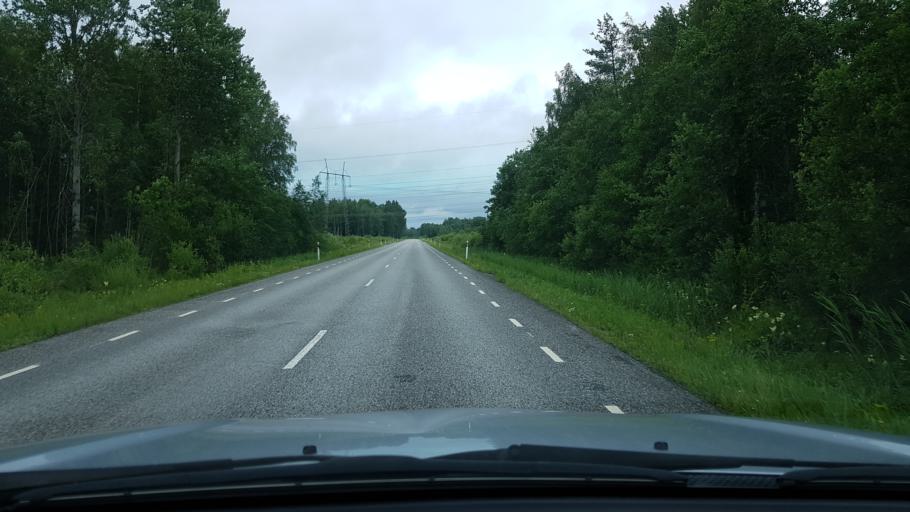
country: EE
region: Ida-Virumaa
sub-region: Narva-Joesuu linn
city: Narva-Joesuu
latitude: 59.3526
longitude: 27.9290
